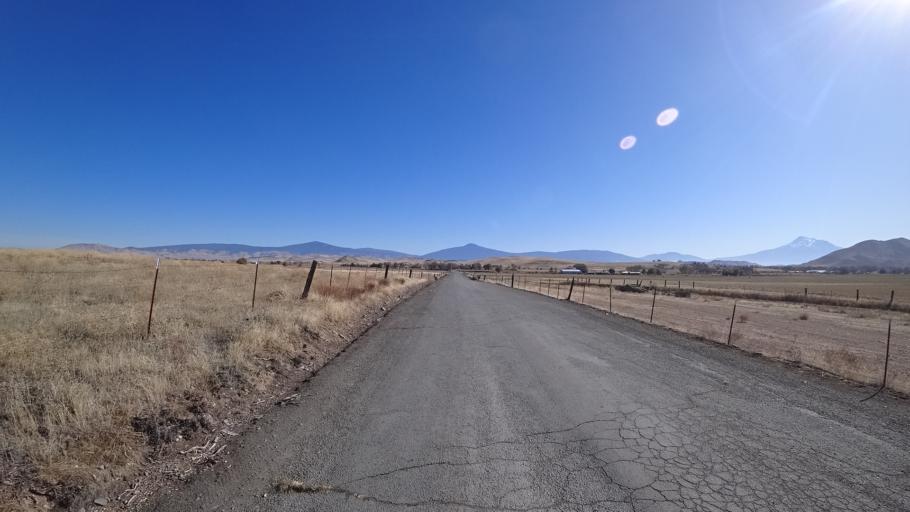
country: US
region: California
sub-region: Siskiyou County
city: Montague
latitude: 41.7423
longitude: -122.5344
